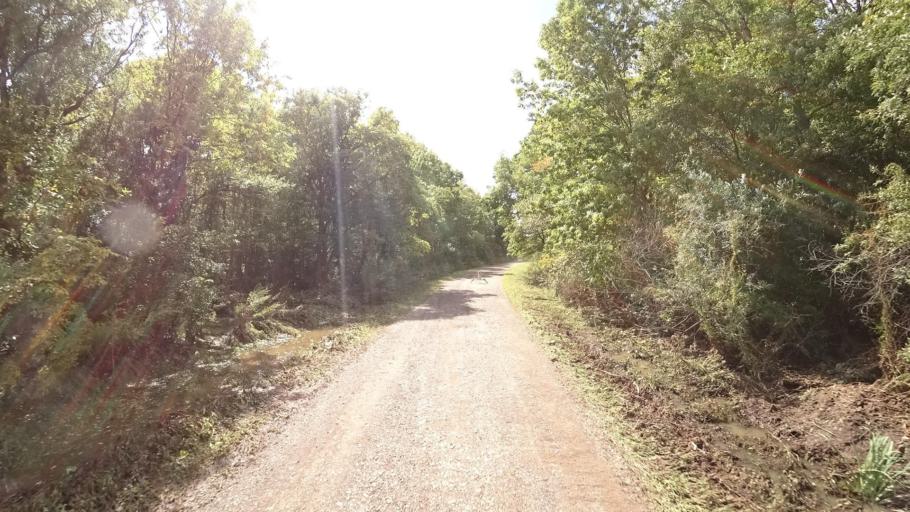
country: RU
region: Primorskiy
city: Yakovlevka
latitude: 44.6609
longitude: 133.7494
